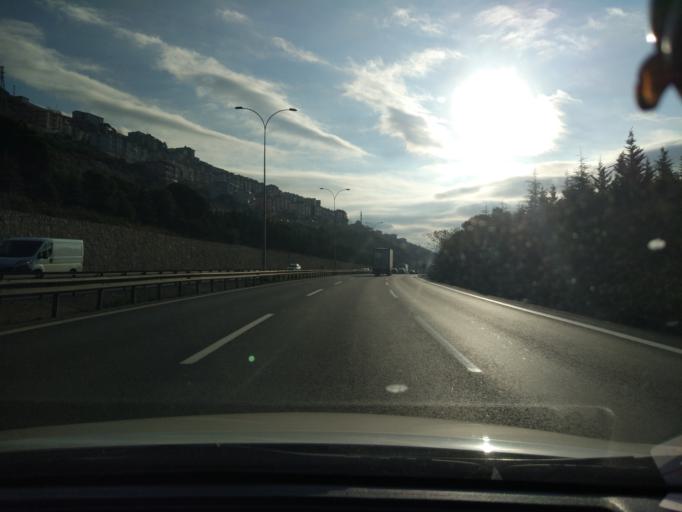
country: TR
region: Kocaeli
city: Hereke
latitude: 40.7877
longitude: 29.6201
